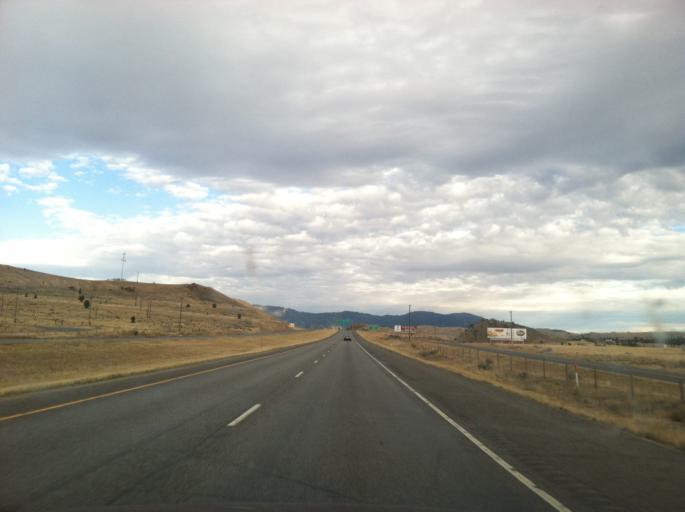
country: US
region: Montana
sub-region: Silver Bow County
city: Butte-Silver Bow (Balance)
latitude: 46.0077
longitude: -112.6640
